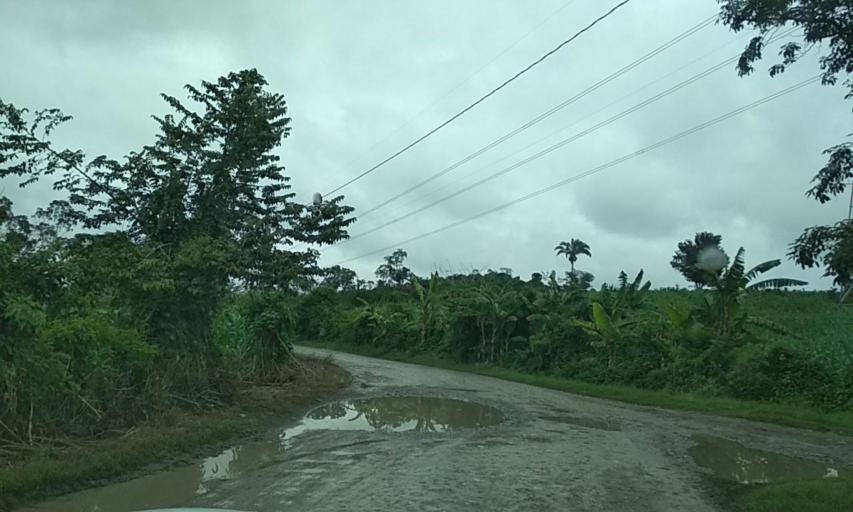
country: MX
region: Puebla
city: Espinal
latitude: 20.3093
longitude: -97.4142
